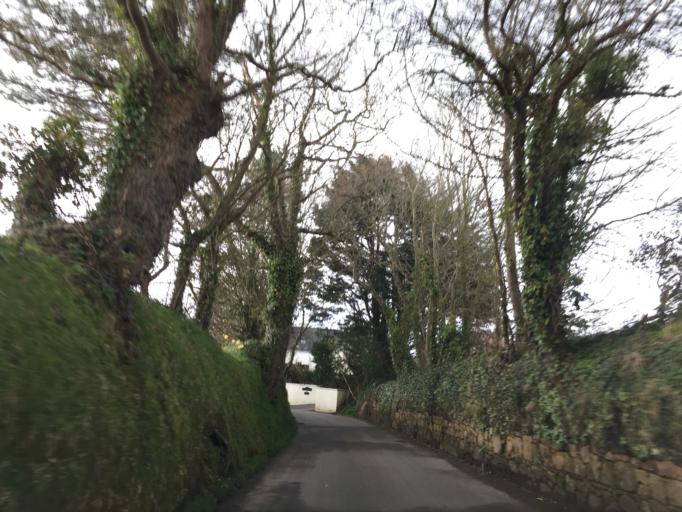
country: JE
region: St Helier
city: Saint Helier
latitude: 49.2057
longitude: -2.1386
